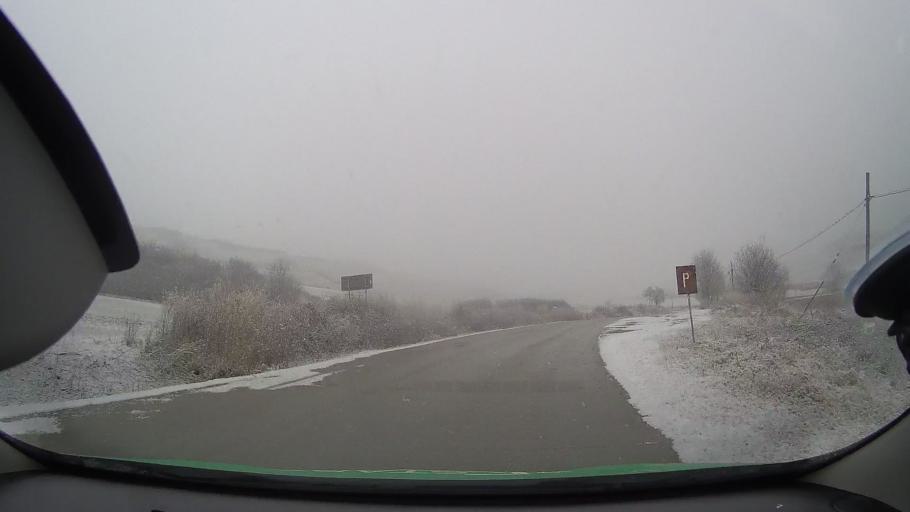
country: RO
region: Alba
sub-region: Comuna Lopadea Noua
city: Lopadea Noua
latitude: 46.3023
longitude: 23.8468
